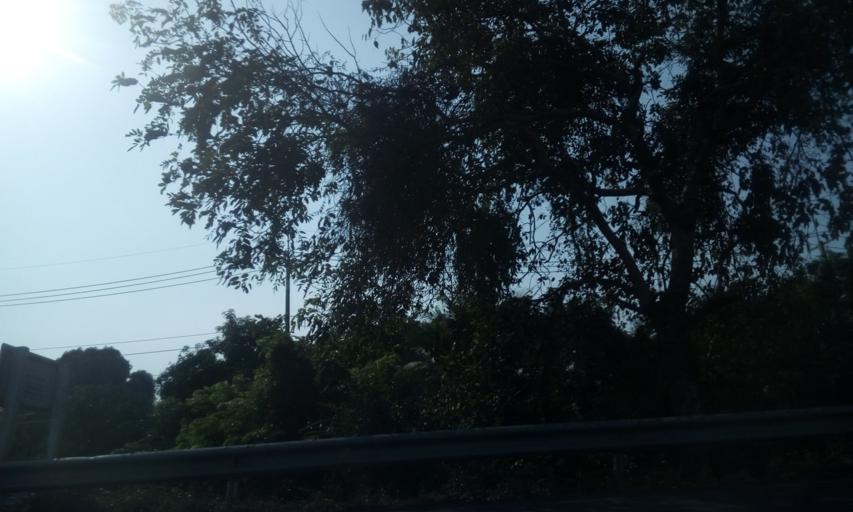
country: TH
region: Sing Buri
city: Phrom Buri
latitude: 14.7807
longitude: 100.4338
